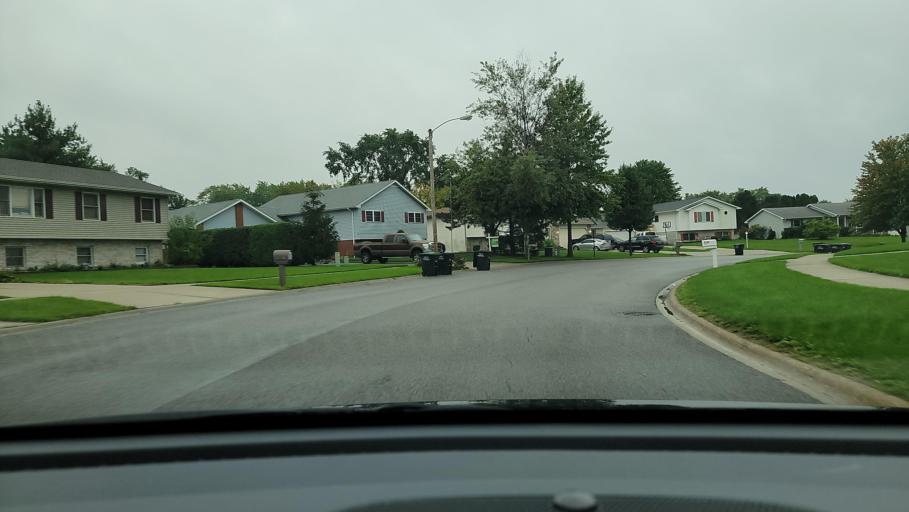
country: US
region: Indiana
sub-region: Porter County
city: Portage
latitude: 41.5623
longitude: -87.1761
